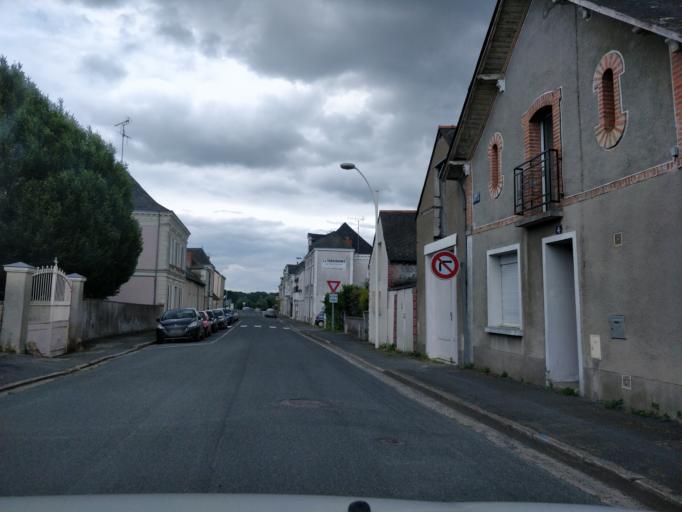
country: FR
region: Pays de la Loire
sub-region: Departement de Maine-et-Loire
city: Grez-Neuville
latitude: 47.6301
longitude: -0.7154
